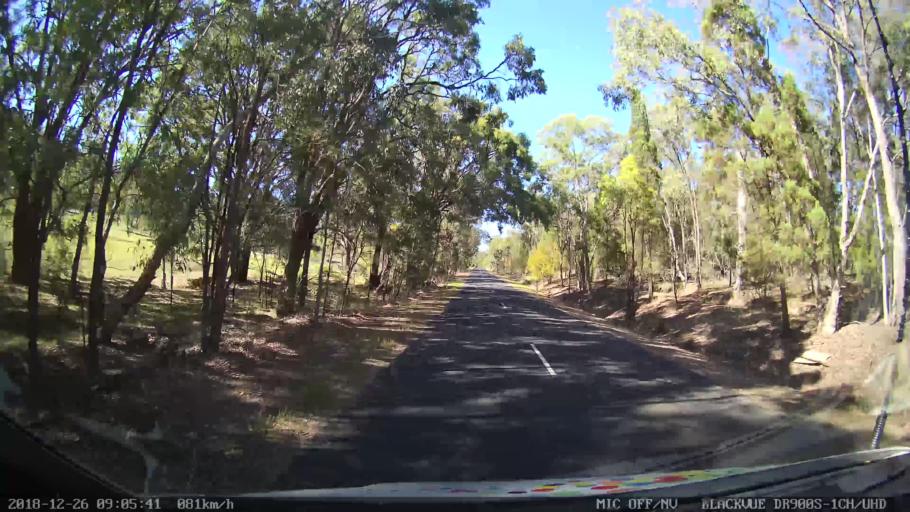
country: AU
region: New South Wales
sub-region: Mid-Western Regional
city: Kandos
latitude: -32.6854
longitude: 150.0061
